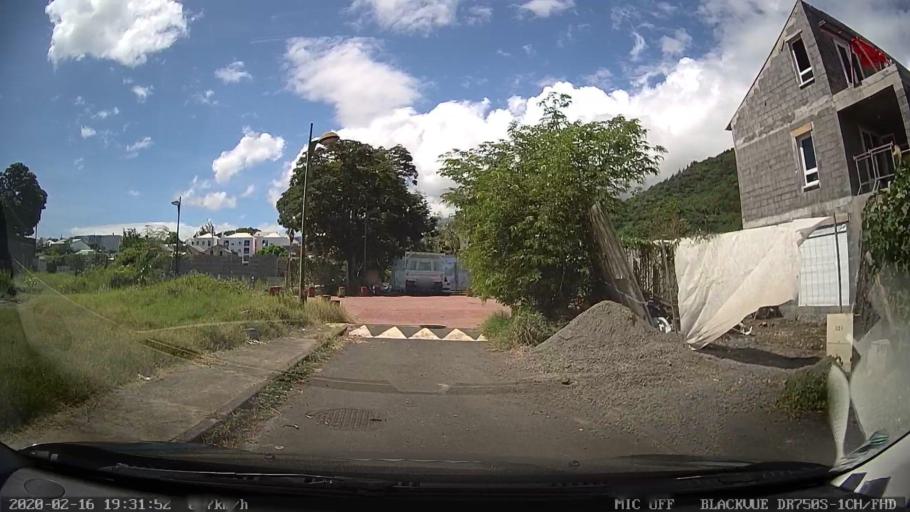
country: RE
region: Reunion
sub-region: Reunion
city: Saint-Denis
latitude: -20.8797
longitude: 55.4408
